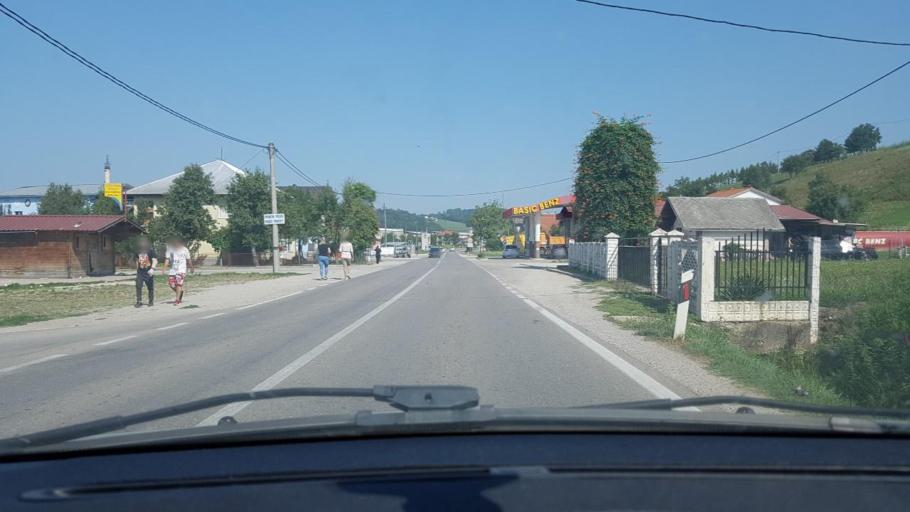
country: BA
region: Federation of Bosnia and Herzegovina
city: Velika Kladusa
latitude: 45.1599
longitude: 15.8218
